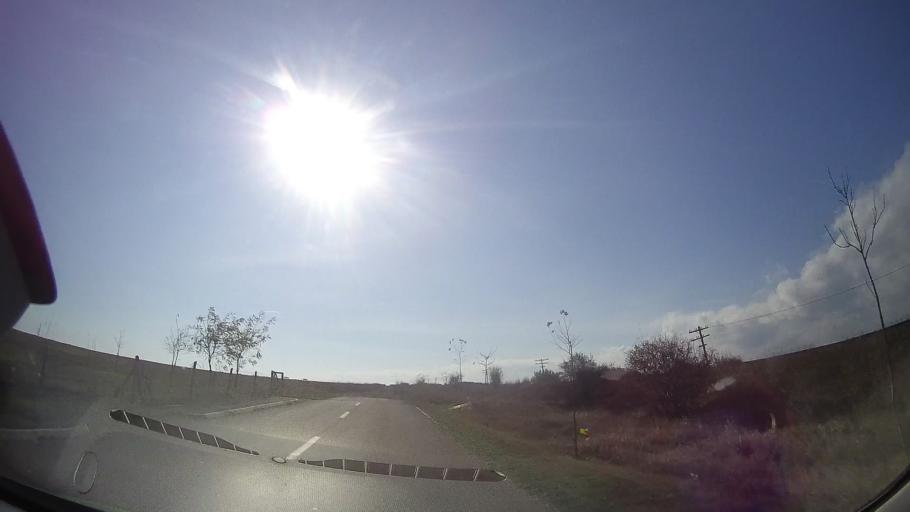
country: RO
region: Constanta
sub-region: Comuna Costinesti
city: Schitu
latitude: 43.9225
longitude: 28.6315
